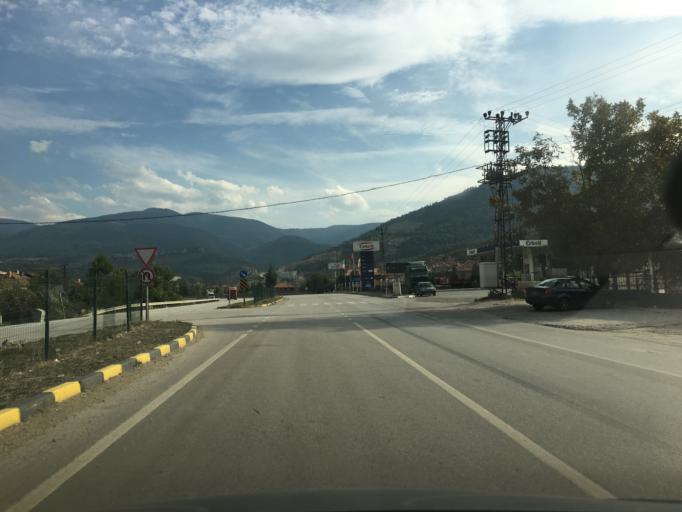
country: TR
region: Karabuk
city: Karabuk
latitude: 41.1047
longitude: 32.6690
